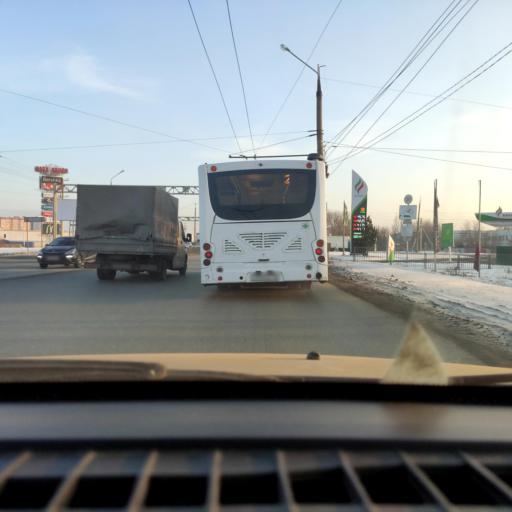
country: RU
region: Samara
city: Tol'yatti
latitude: 53.5455
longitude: 49.3818
